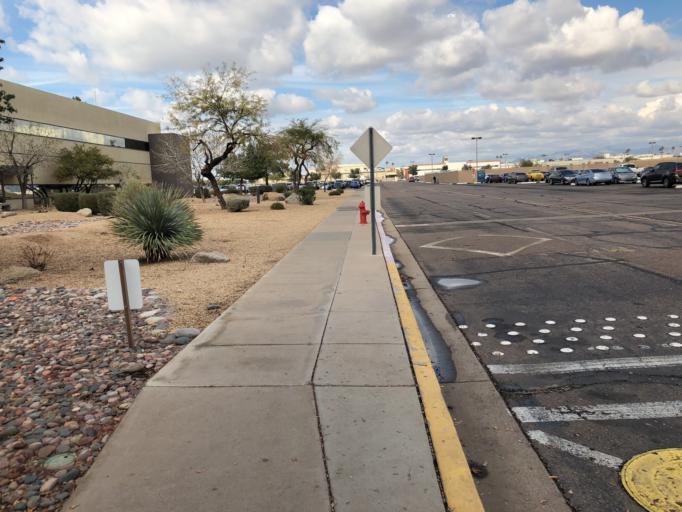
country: US
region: Arizona
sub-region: Maricopa County
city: Tempe
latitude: 33.4600
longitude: -111.9040
